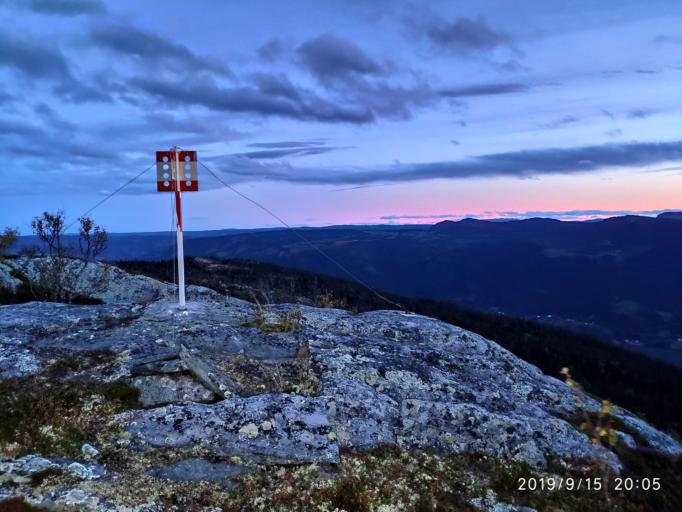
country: NO
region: Oppland
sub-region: Oyer
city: Tretten
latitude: 61.4245
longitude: 10.2605
